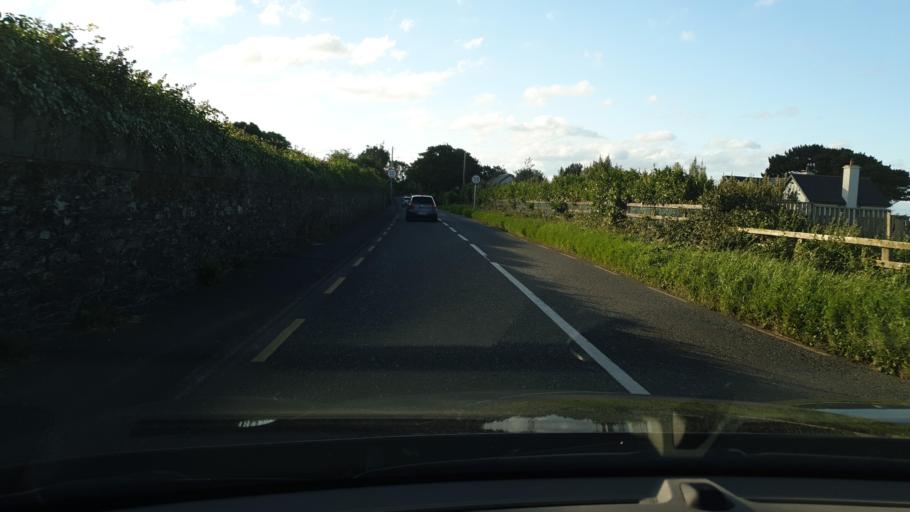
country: IE
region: Leinster
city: Balbriggan
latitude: 53.6011
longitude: -6.1656
